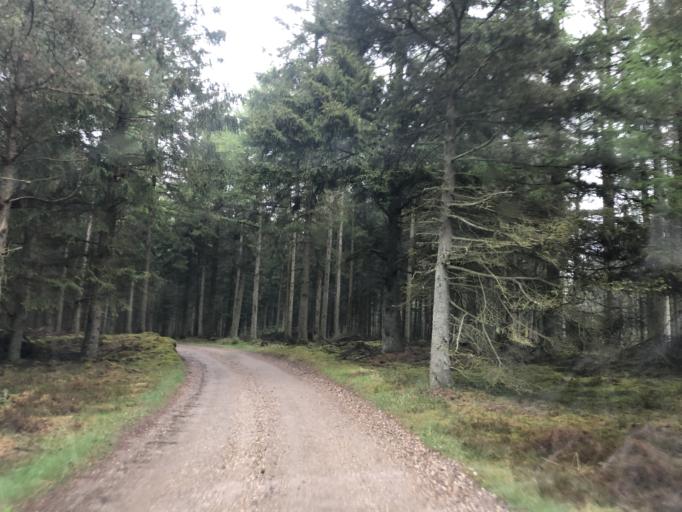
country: DK
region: Central Jutland
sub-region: Lemvig Kommune
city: Lemvig
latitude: 56.4551
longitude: 8.3956
